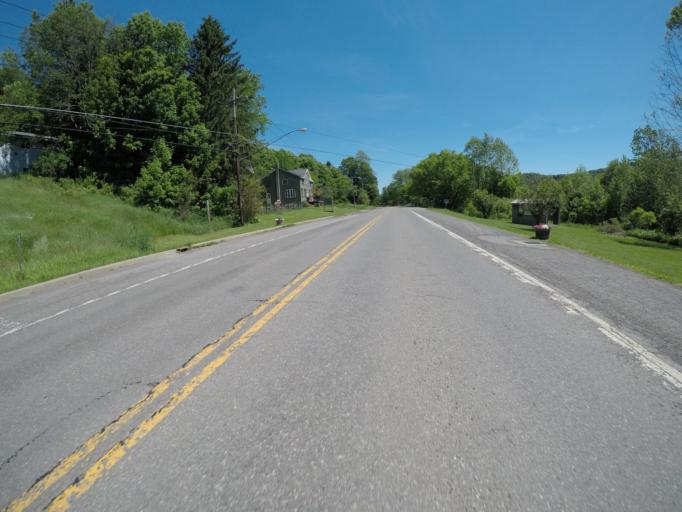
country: US
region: New York
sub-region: Delaware County
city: Delhi
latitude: 42.1954
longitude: -74.9897
